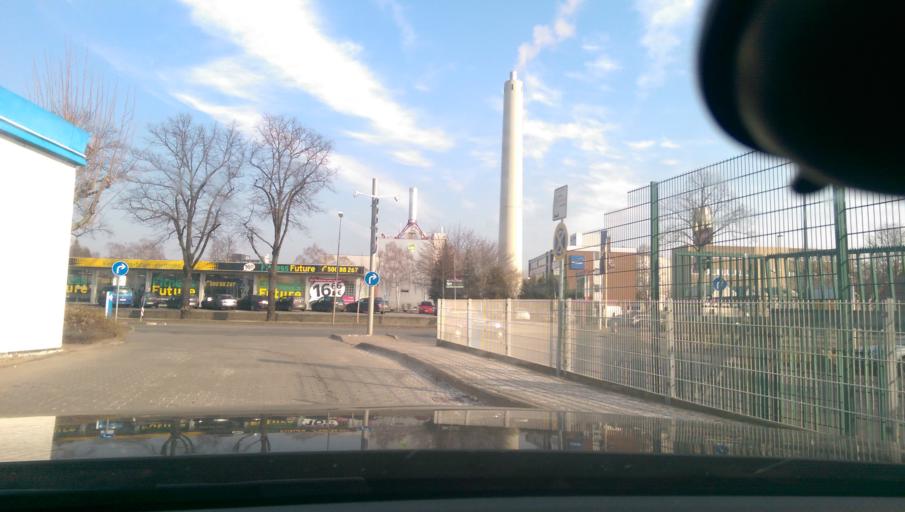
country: DE
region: Lower Saxony
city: Goettingen
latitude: 51.5537
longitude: 9.9308
